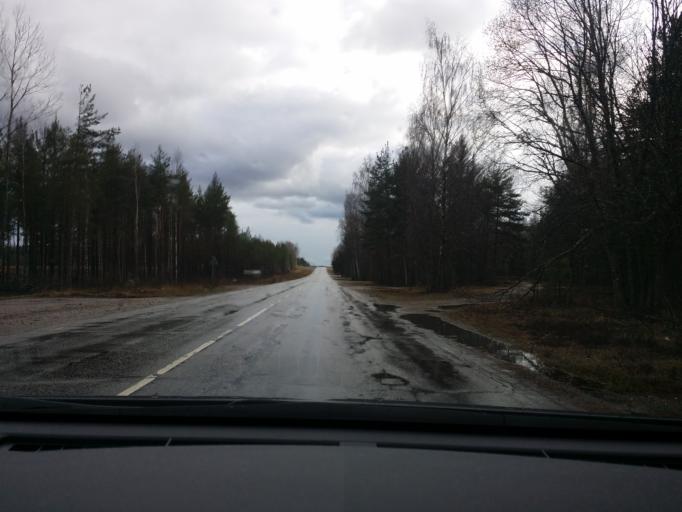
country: SE
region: Soedermanland
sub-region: Eskilstuna Kommun
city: Arla
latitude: 59.3382
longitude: 16.6903
